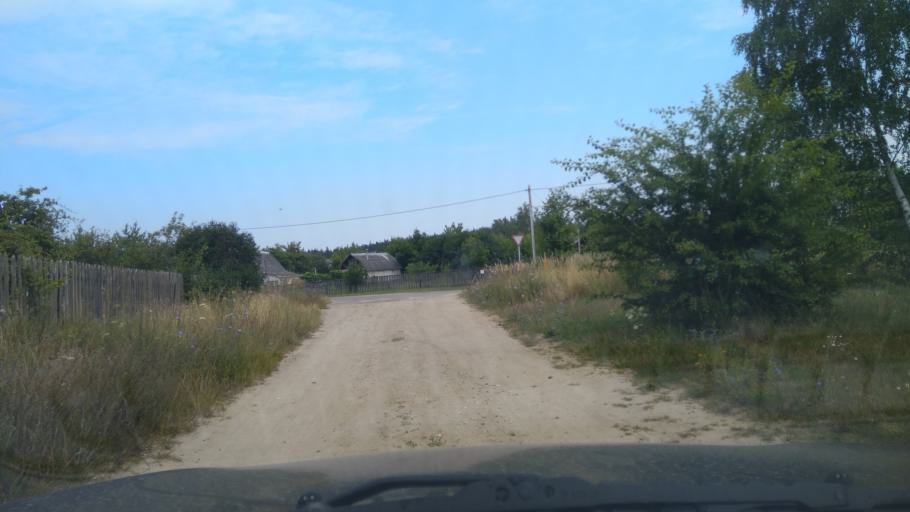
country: BY
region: Brest
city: Nyakhachava
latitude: 52.6084
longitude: 25.0921
